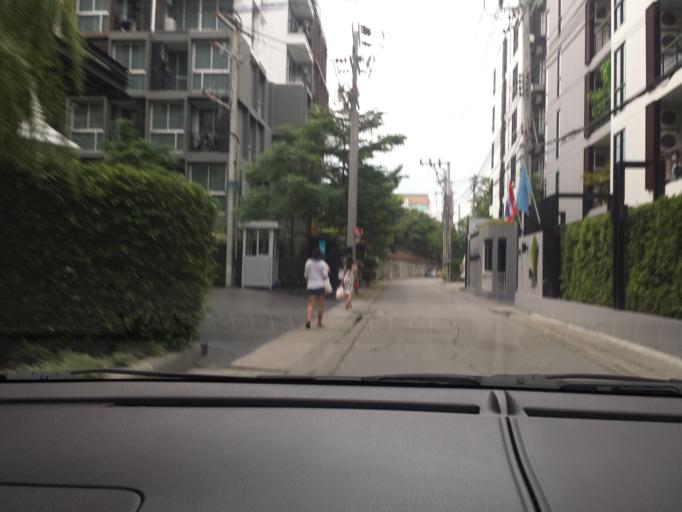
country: TH
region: Bangkok
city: Phra Khanong
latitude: 13.7042
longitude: 100.5993
